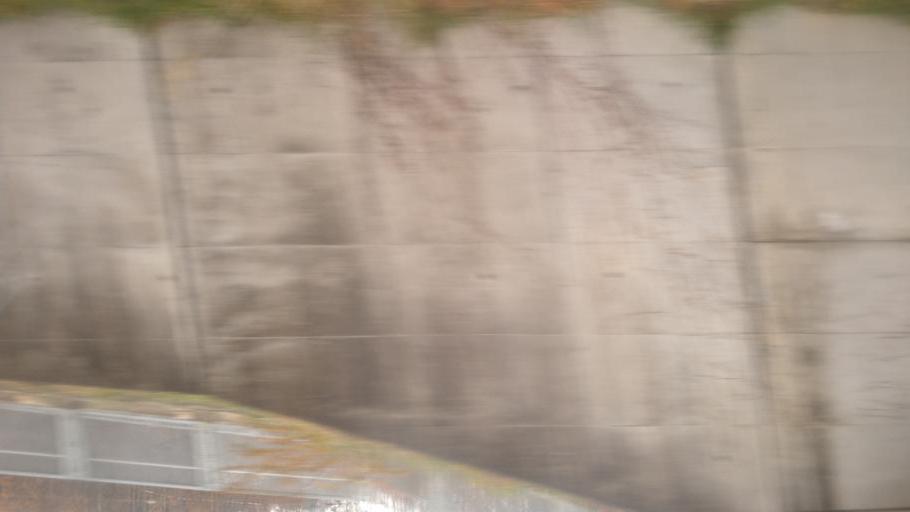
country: JP
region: Nagano
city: Hotaka
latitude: 36.3560
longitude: 137.9327
